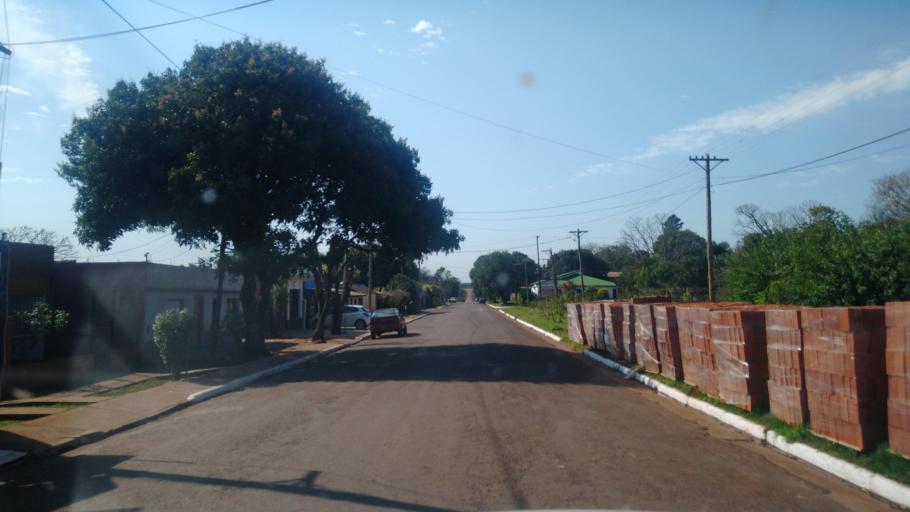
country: AR
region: Misiones
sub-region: Departamento de San Ignacio
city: San Ignacio
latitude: -27.2543
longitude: -55.5370
